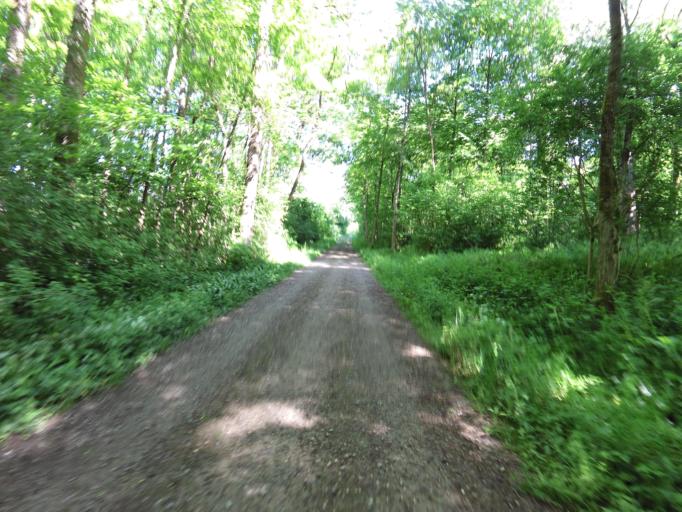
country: CH
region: Thurgau
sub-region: Frauenfeld District
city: Mullheim
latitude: 47.5873
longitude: 9.0033
